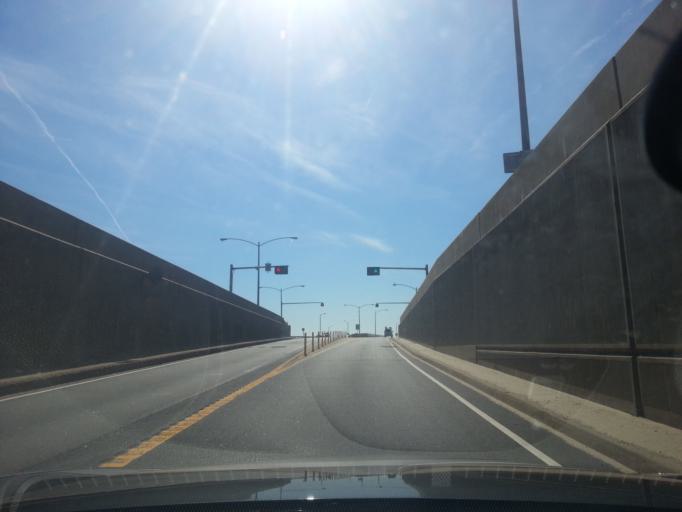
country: US
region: Virginia
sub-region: City of Virginia Beach
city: Virginia Beach
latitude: 37.0353
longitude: -76.0783
